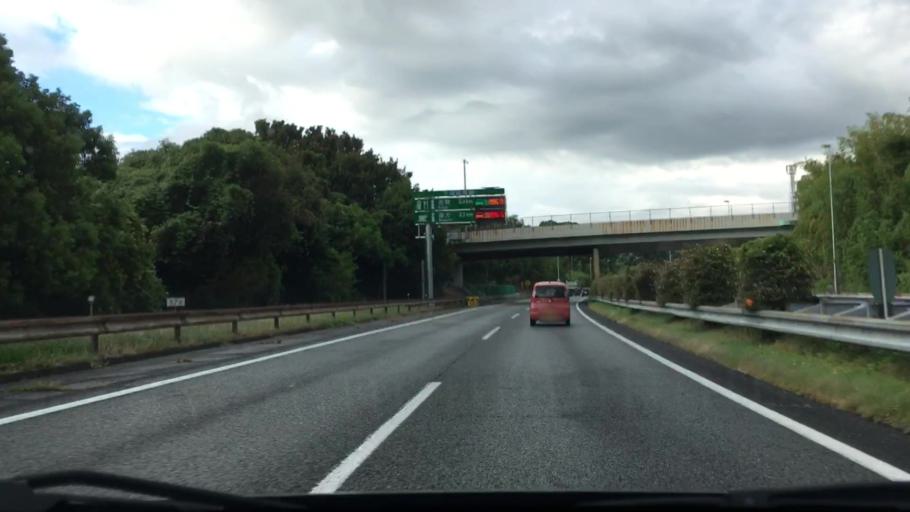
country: JP
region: Fukuoka
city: Koga
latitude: 33.7180
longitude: 130.4926
